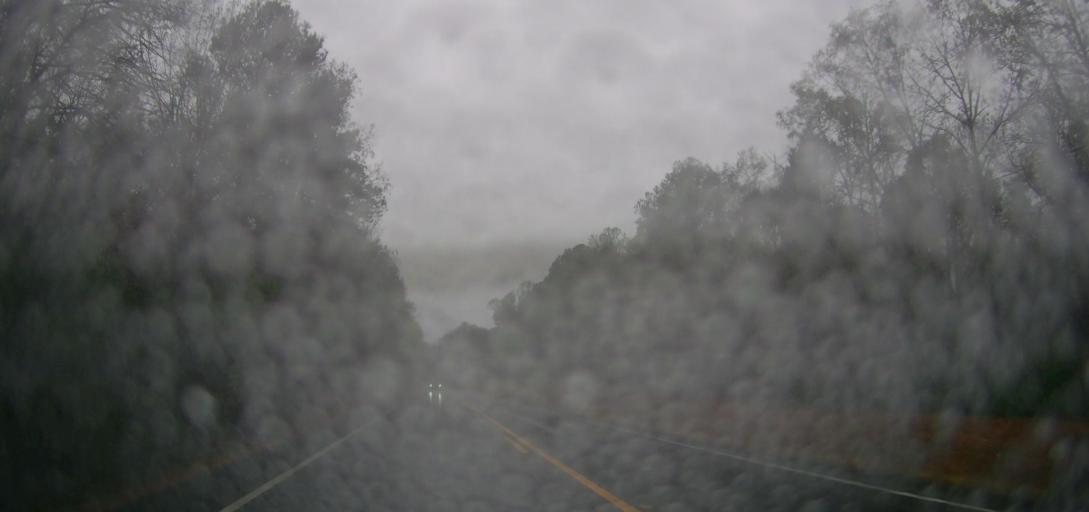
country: US
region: Georgia
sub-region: Putnam County
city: Eatonton
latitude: 33.2127
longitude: -83.4333
